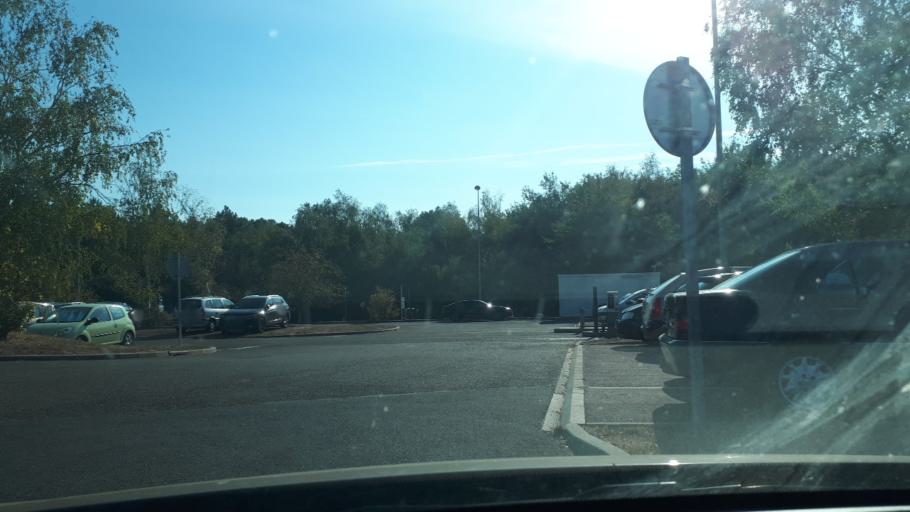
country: FR
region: Centre
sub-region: Departement du Loir-et-Cher
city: Naveil
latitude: 47.8213
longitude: 1.0214
